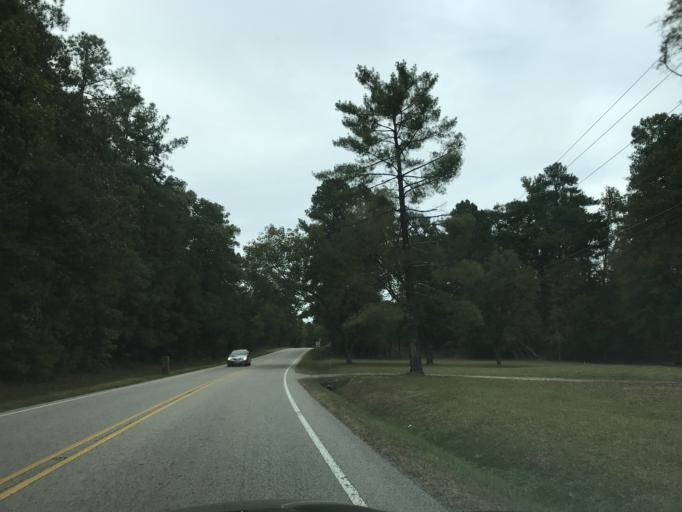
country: US
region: North Carolina
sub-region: Wake County
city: Knightdale
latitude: 35.8406
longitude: -78.5160
